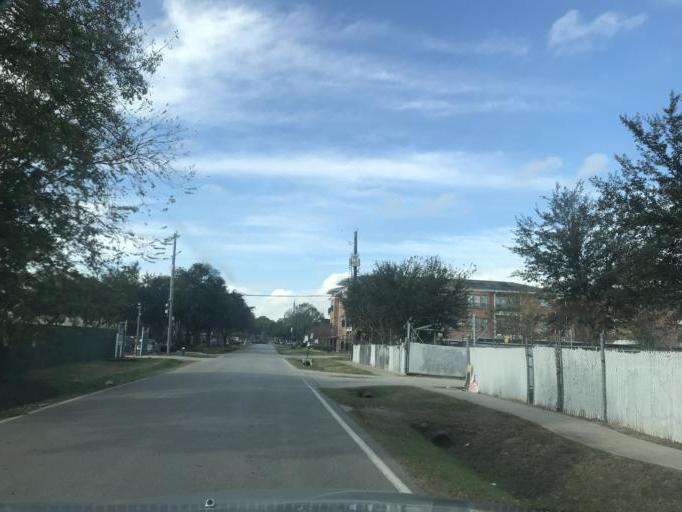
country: US
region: Texas
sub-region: Harris County
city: Hunters Creek Village
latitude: 29.7354
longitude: -95.4862
